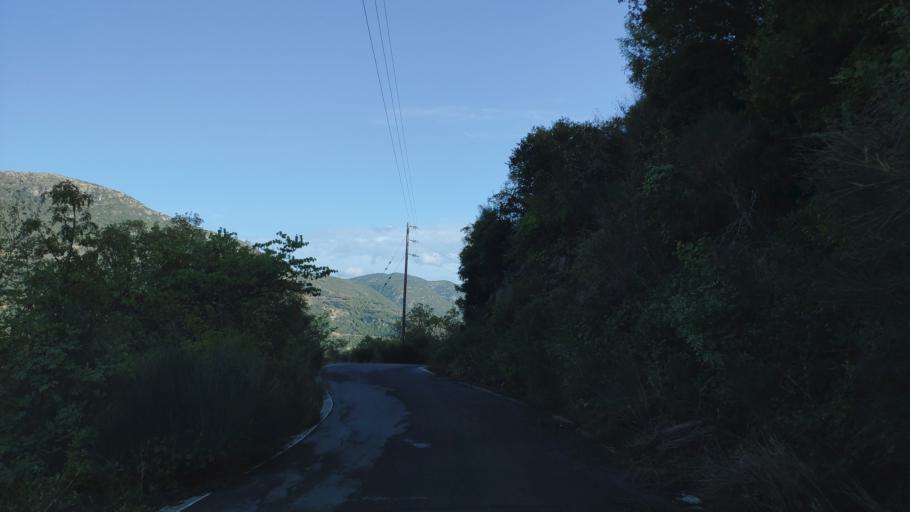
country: GR
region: Peloponnese
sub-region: Nomos Arkadias
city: Dimitsana
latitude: 37.5587
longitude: 22.0383
